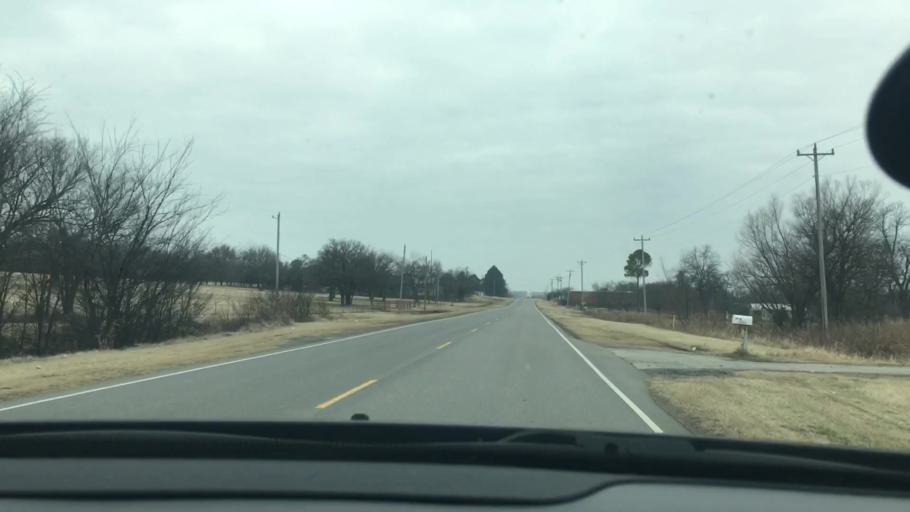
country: US
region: Oklahoma
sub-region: Carter County
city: Healdton
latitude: 34.2564
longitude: -97.4923
